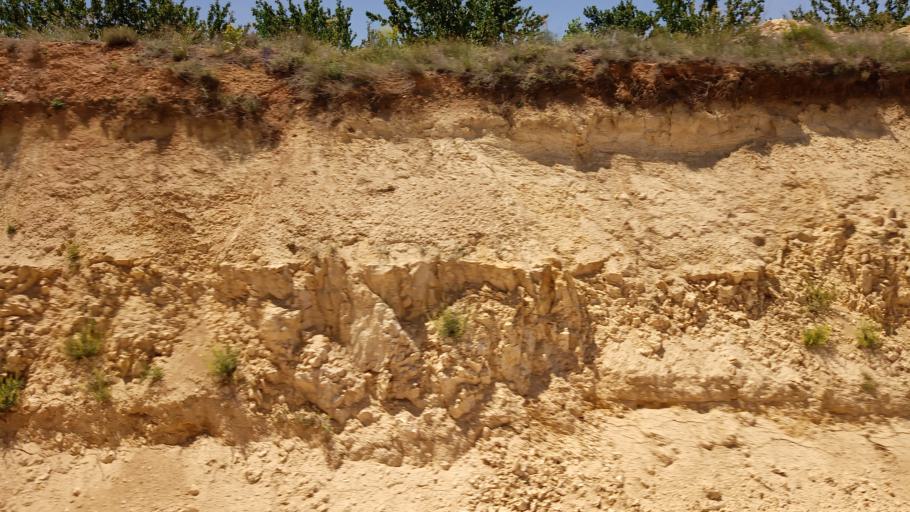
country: TR
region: Malatya
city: Darende
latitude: 38.6337
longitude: 37.4539
